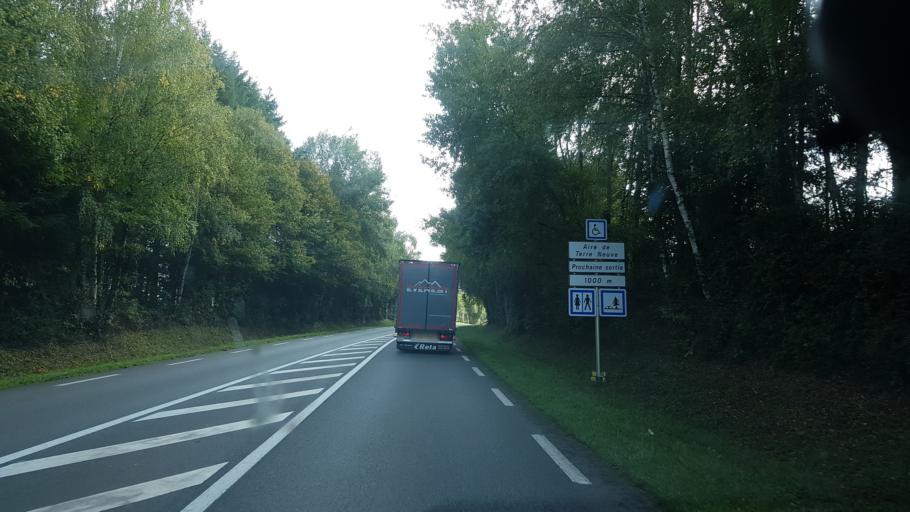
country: FR
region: Poitou-Charentes
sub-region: Departement de la Charente
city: Confolens
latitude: 46.0319
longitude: 0.6589
